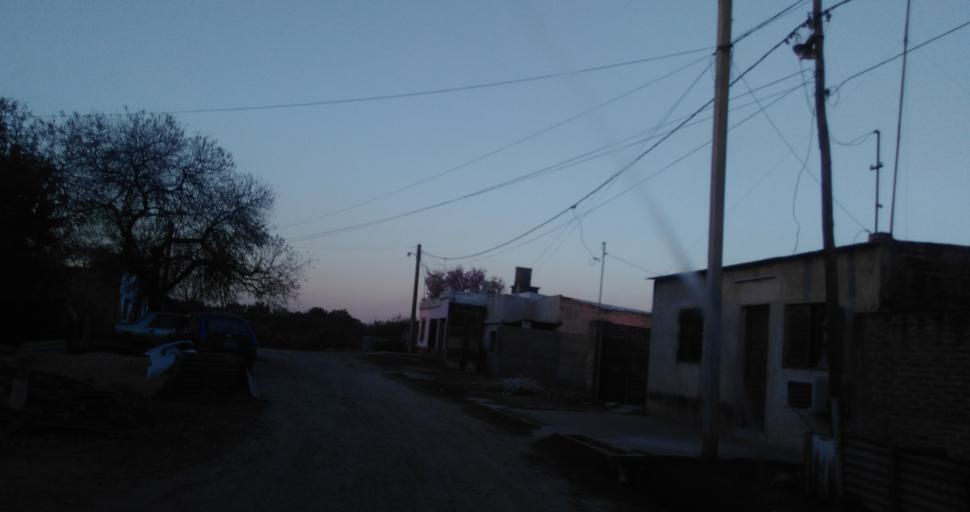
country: AR
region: Chaco
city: Resistencia
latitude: -27.4299
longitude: -58.9923
